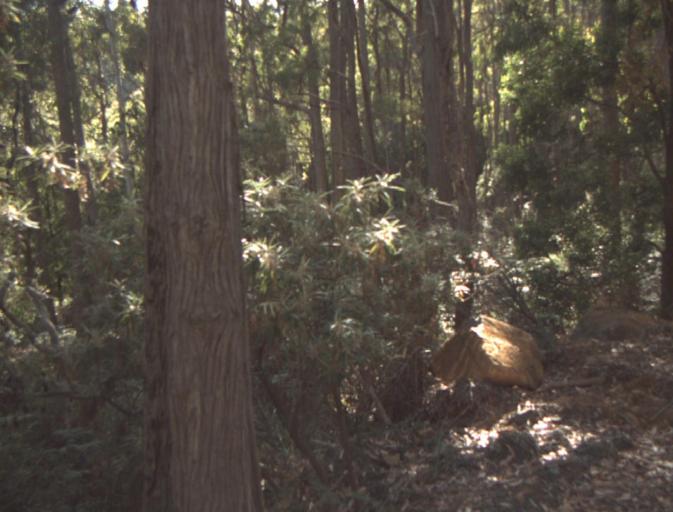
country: AU
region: Tasmania
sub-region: Launceston
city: Mayfield
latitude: -41.2971
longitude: 147.1853
